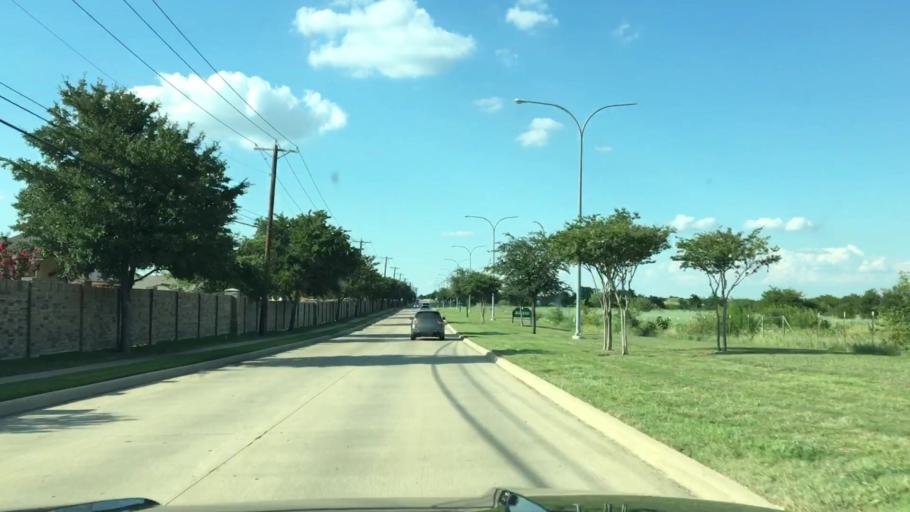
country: US
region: Texas
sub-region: Tarrant County
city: Haslet
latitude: 32.9742
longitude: -97.3816
